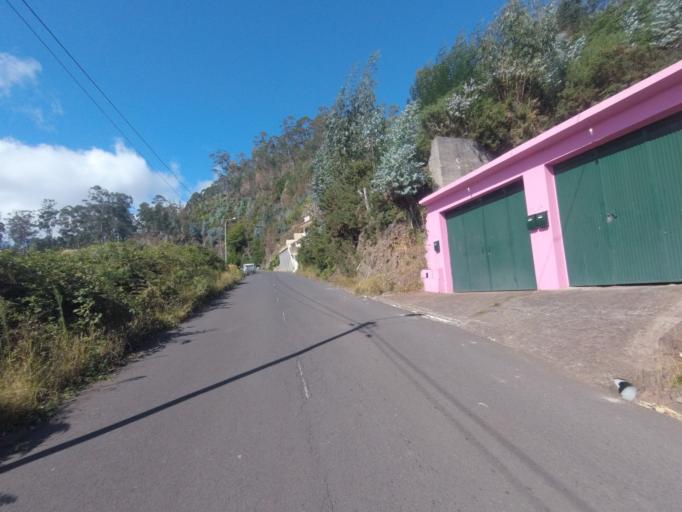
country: PT
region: Madeira
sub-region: Ribeira Brava
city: Campanario
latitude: 32.6853
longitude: -17.0218
